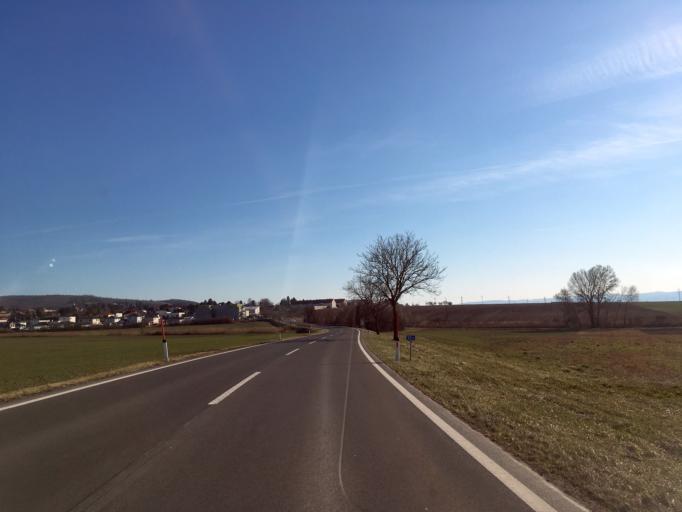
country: AT
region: Burgenland
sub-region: Eisenstadt-Umgebung
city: Hornstein
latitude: 47.8926
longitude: 16.4382
